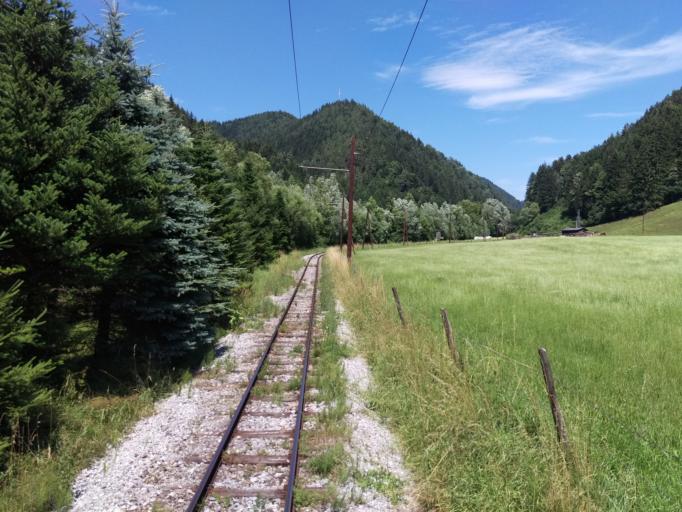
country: AT
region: Styria
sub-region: Politischer Bezirk Bruck-Muerzzuschlag
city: Pernegg an der Mur
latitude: 47.3572
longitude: 15.3690
